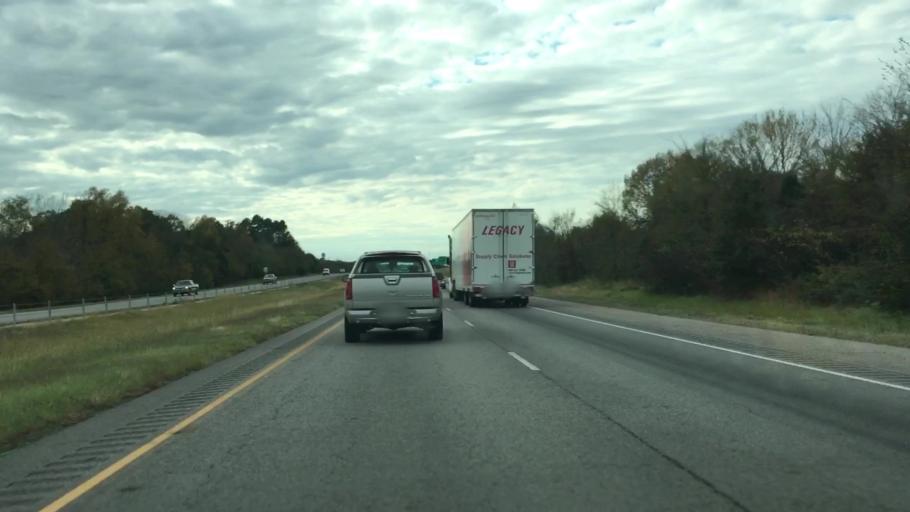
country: US
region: Arkansas
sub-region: Conway County
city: Morrilton
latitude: 35.1633
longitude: -92.6319
